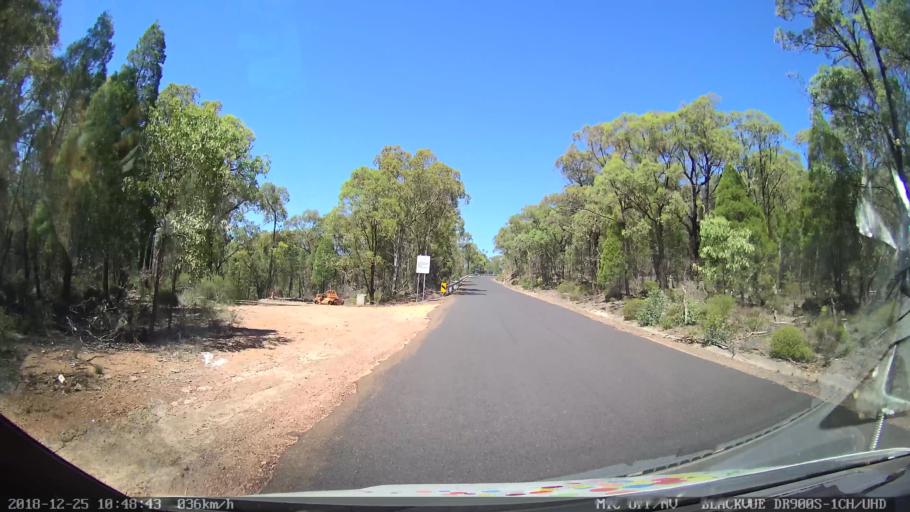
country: AU
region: New South Wales
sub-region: Upper Hunter Shire
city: Merriwa
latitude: -32.4481
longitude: 150.2737
